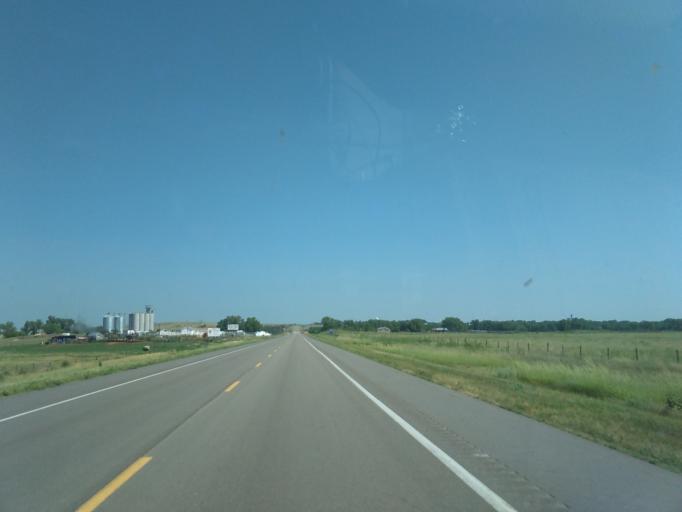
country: US
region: Nebraska
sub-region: Dundy County
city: Benkelman
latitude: 40.0291
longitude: -101.5430
